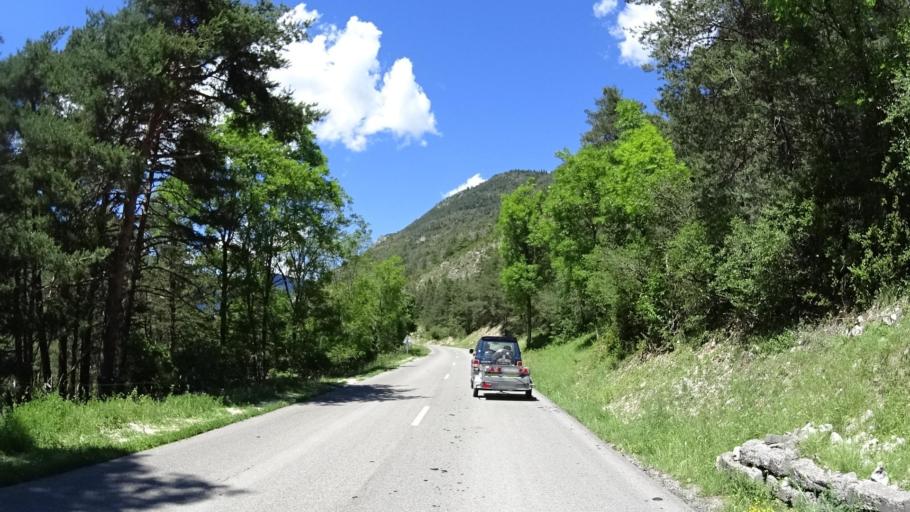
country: FR
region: Provence-Alpes-Cote d'Azur
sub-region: Departement des Alpes-de-Haute-Provence
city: Annot
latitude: 44.0651
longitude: 6.5747
